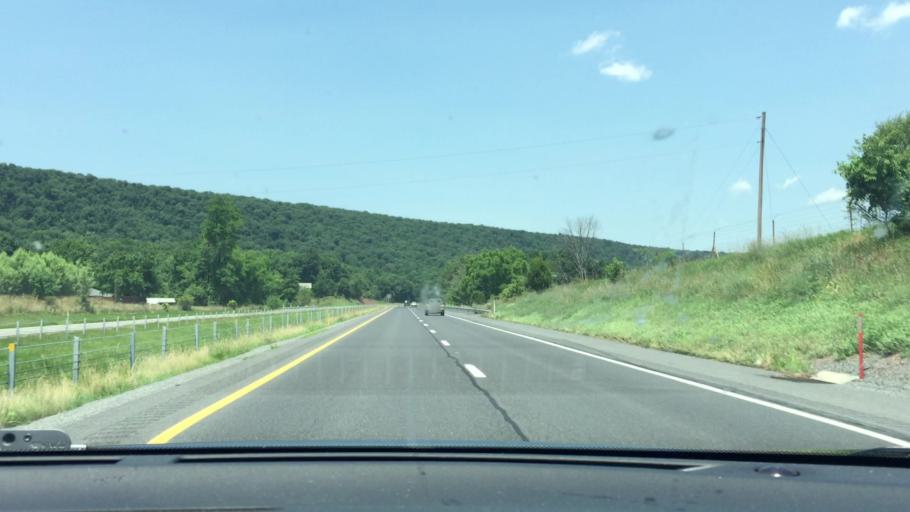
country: US
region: Maryland
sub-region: Washington County
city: Hancock
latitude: 39.8321
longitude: -78.2749
